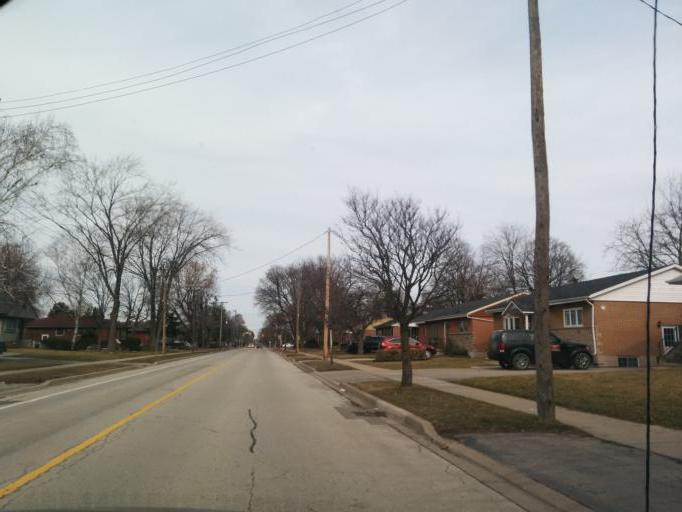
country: CA
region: Ontario
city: Burlington
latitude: 43.3388
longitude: -79.8029
